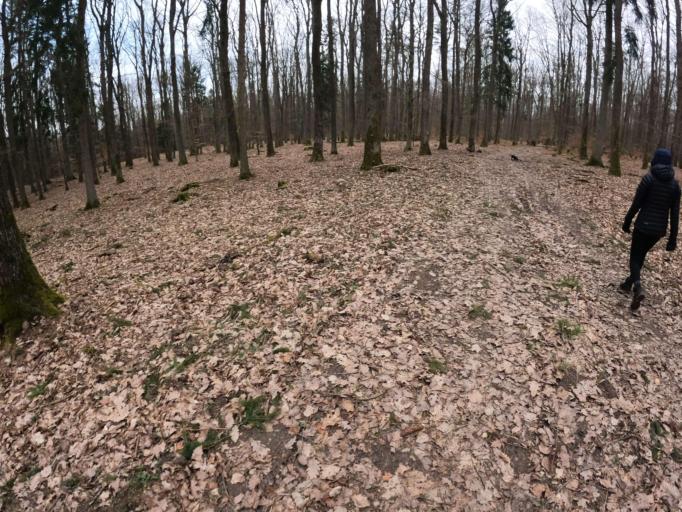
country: PL
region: West Pomeranian Voivodeship
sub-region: Powiat kamienski
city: Golczewo
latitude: 53.8103
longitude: 15.0185
